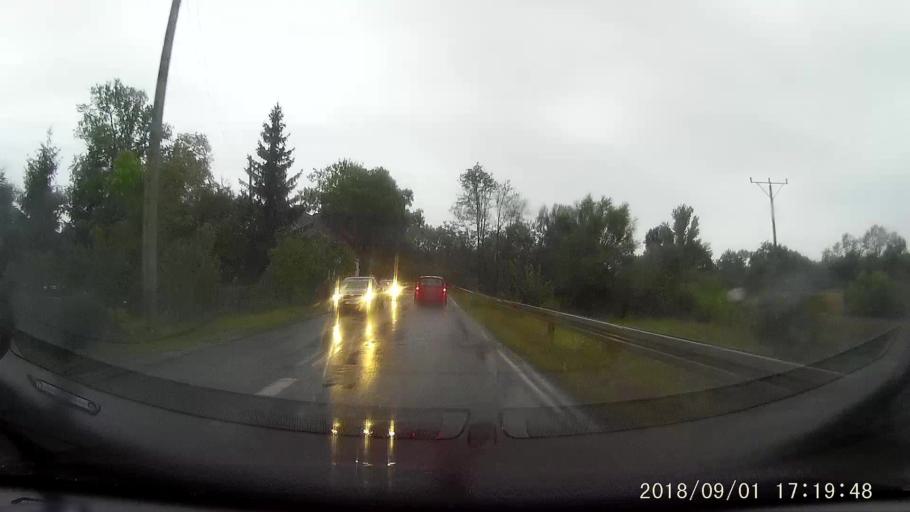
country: PL
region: Lubusz
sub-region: Powiat zielonogorski
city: Nowogrod Bobrzanski
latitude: 51.7292
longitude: 15.2744
